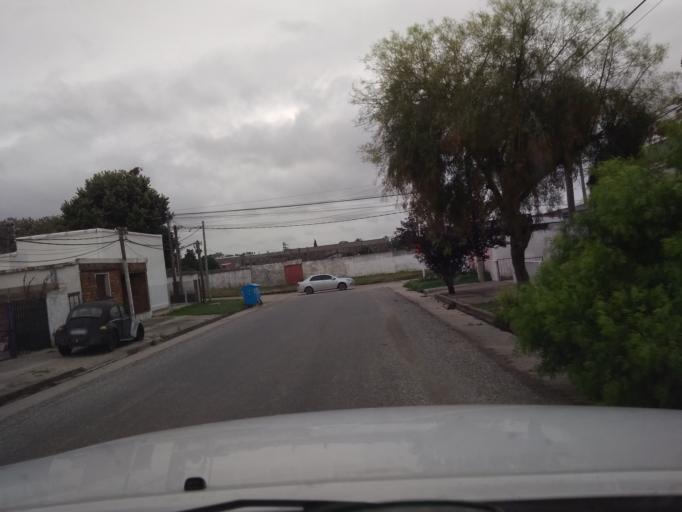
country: UY
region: Florida
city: Florida
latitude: -34.1056
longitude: -56.2088
